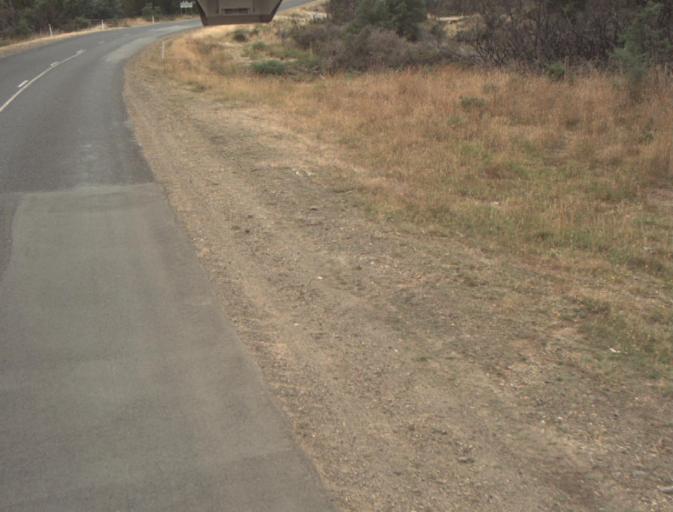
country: AU
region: Tasmania
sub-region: Northern Midlands
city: Evandale
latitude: -41.5107
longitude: 147.3438
